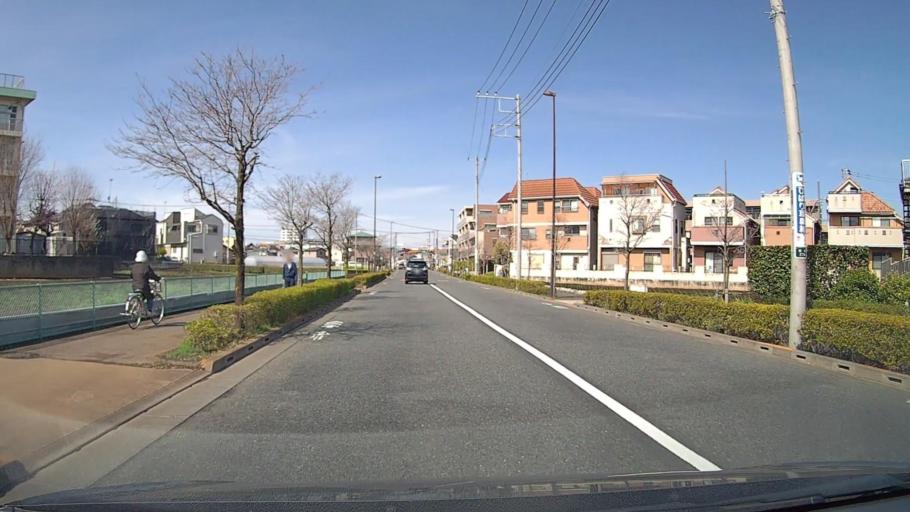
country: JP
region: Tokyo
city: Tanashicho
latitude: 35.7525
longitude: 139.5540
